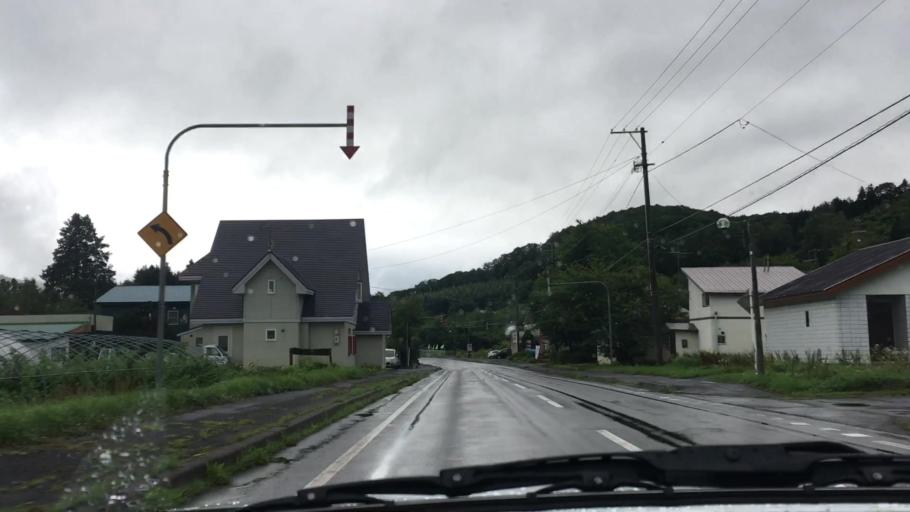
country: JP
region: Hokkaido
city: Niseko Town
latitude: 42.6463
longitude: 140.7336
